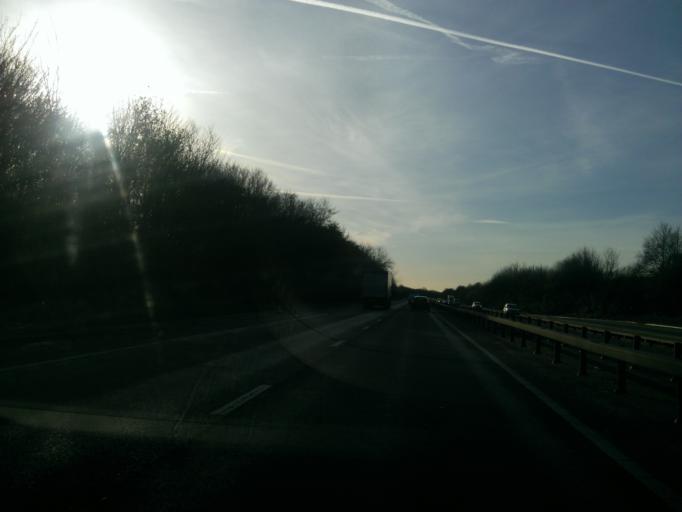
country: GB
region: England
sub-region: Essex
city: Witham
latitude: 51.8004
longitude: 0.6522
